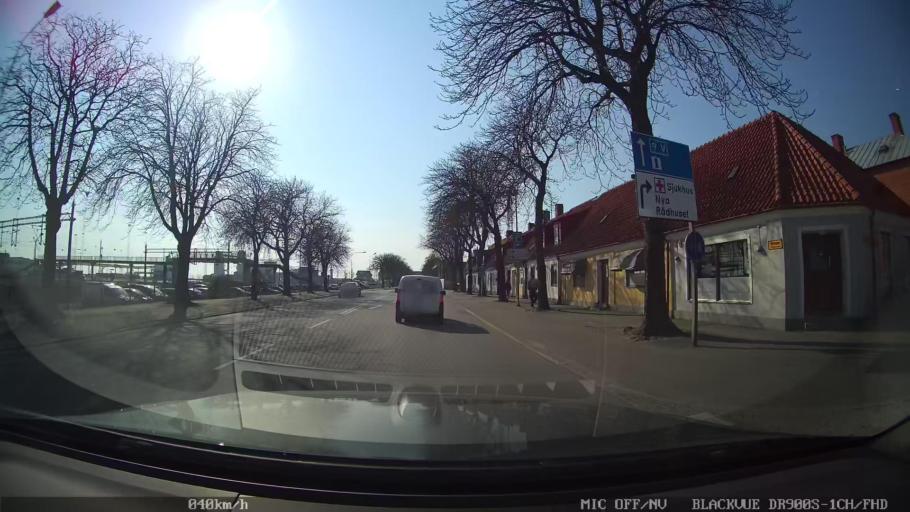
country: SE
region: Skane
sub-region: Ystads Kommun
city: Ystad
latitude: 55.4283
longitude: 13.8308
